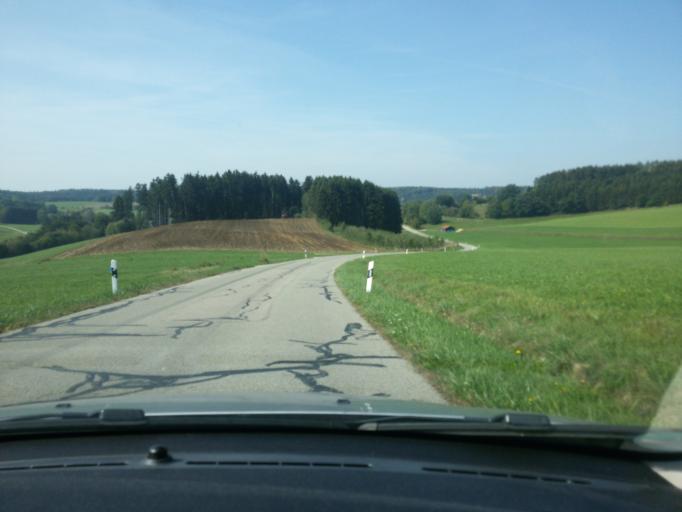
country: DE
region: Bavaria
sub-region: Swabia
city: Walkertshofen
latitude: 48.2199
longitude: 10.6039
